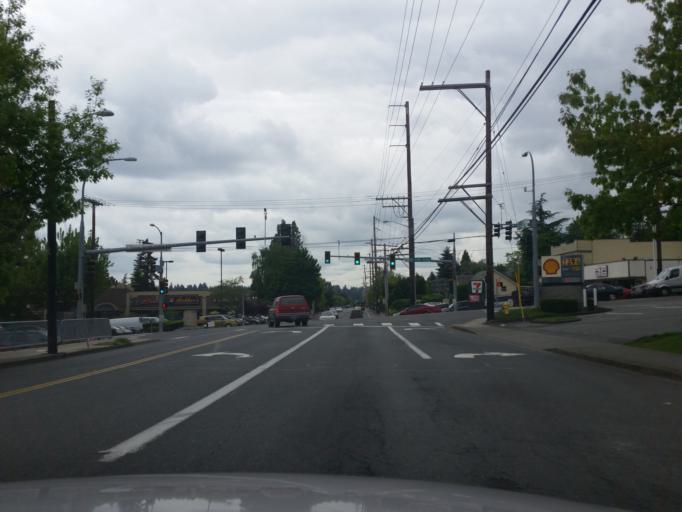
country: US
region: Washington
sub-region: King County
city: Kirkland
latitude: 47.6663
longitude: -122.1962
